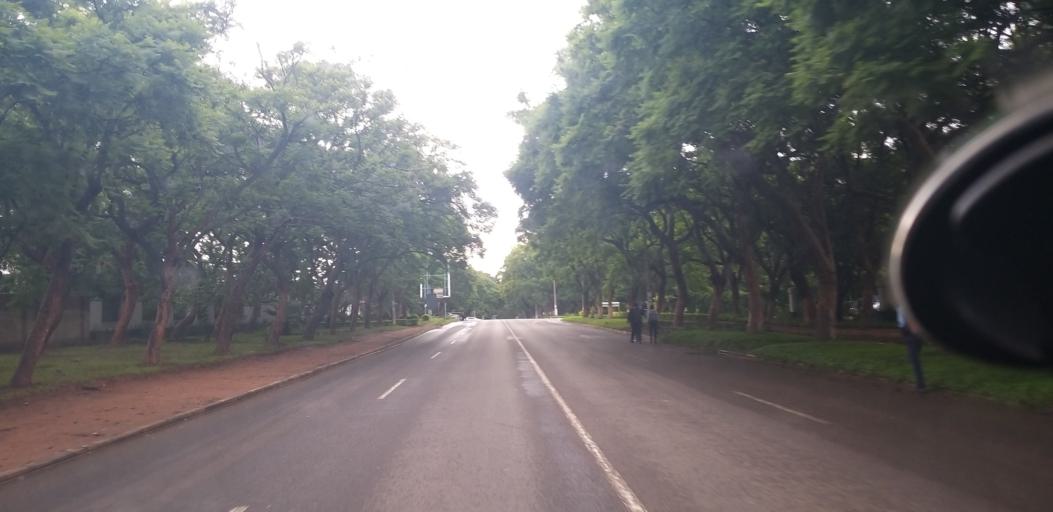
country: ZM
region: Lusaka
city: Lusaka
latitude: -15.4161
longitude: 28.3020
